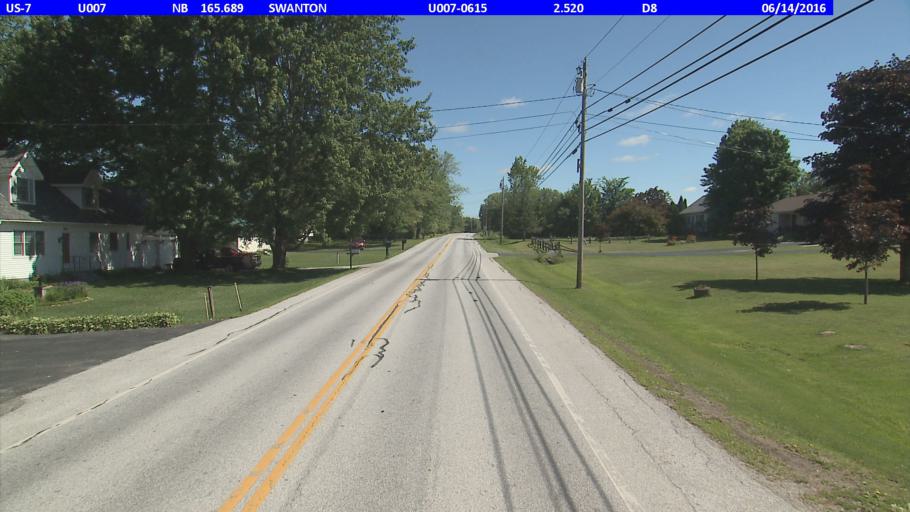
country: US
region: Vermont
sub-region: Franklin County
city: Swanton
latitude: 44.8832
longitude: -73.0944
